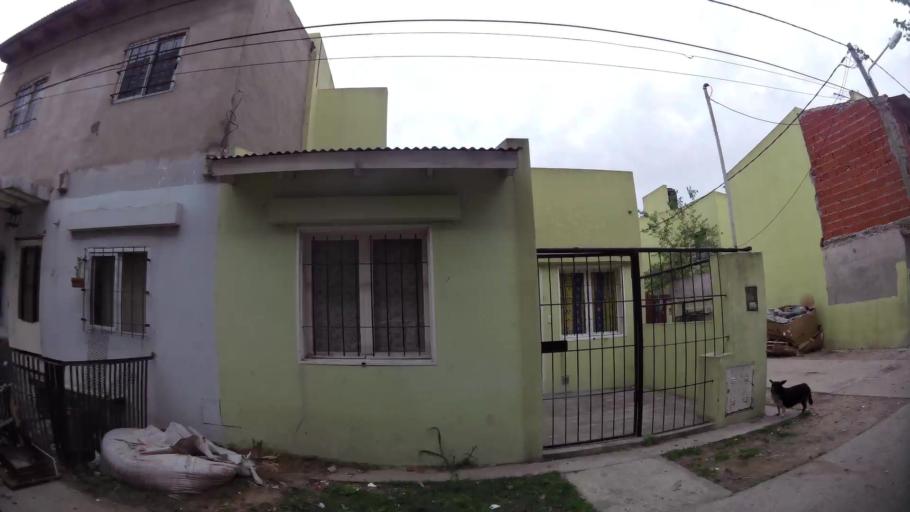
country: AR
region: Buenos Aires
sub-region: Partido de Avellaneda
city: Avellaneda
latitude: -34.6499
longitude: -58.3586
